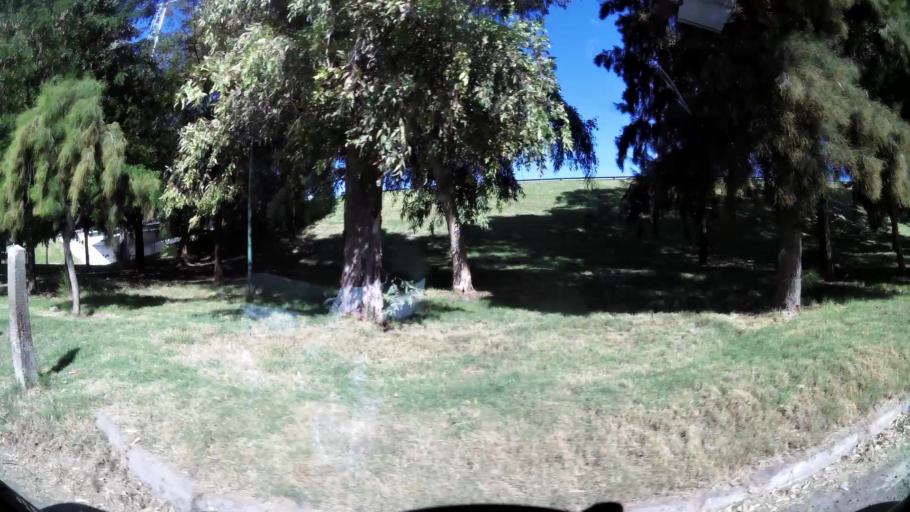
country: AR
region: San Juan
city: San Juan
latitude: -31.5206
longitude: -68.5376
